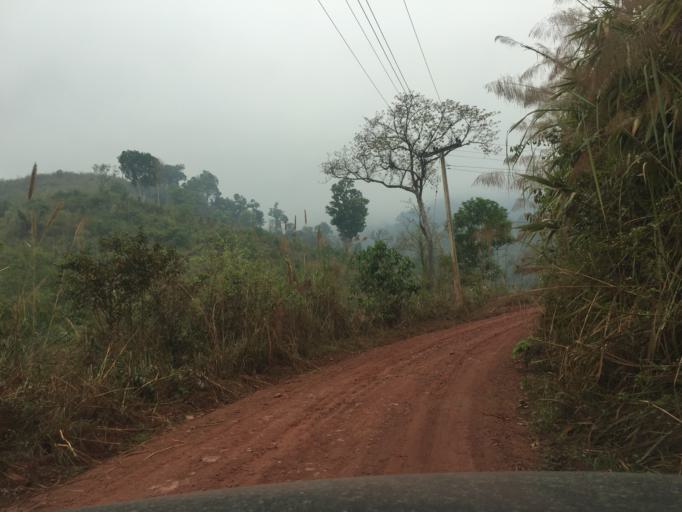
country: TH
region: Nan
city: Bo Kluea
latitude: 18.8643
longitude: 101.4352
